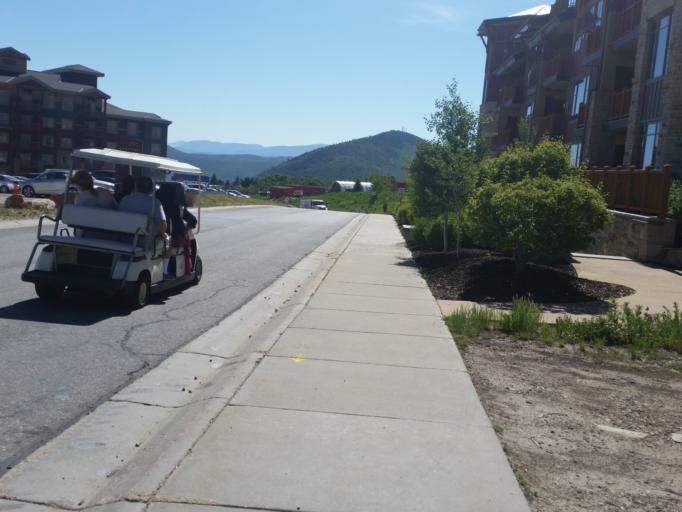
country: US
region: Utah
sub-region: Summit County
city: Snyderville
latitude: 40.6831
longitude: -111.5561
